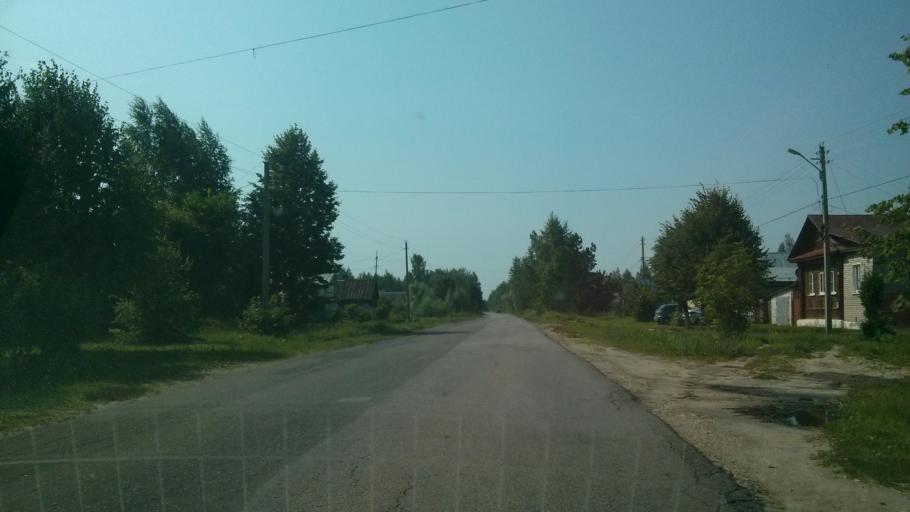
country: RU
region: Vladimir
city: Murom
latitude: 55.5342
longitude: 42.0241
